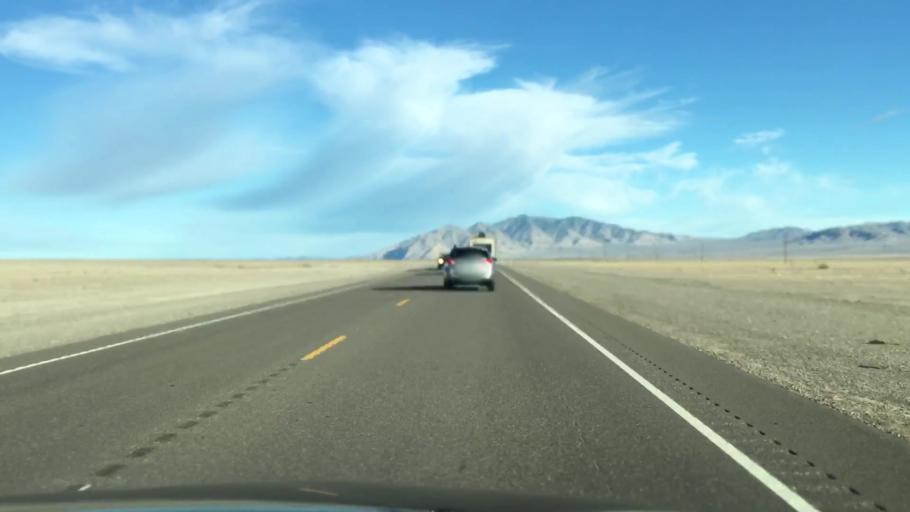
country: US
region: Nevada
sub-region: Nye County
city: Tonopah
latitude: 38.0178
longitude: -117.7901
